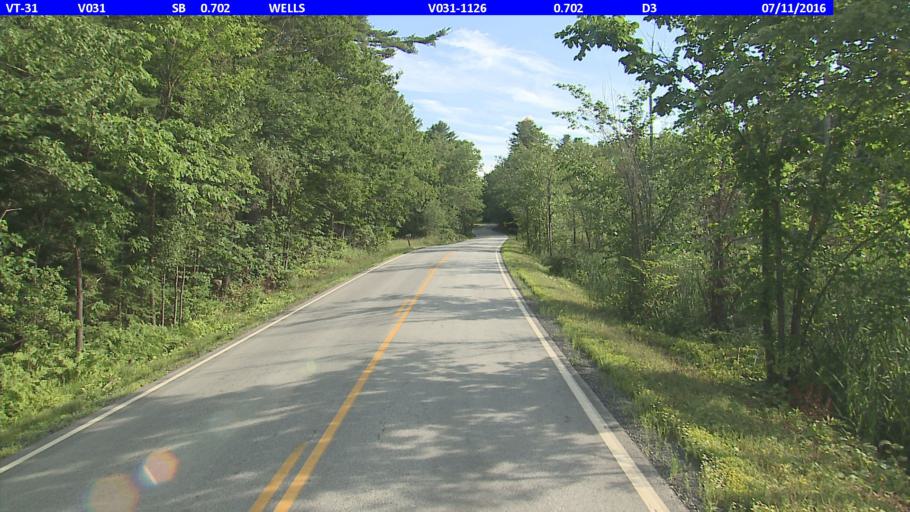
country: US
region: New York
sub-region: Washington County
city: Granville
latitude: 43.4476
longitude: -73.2449
